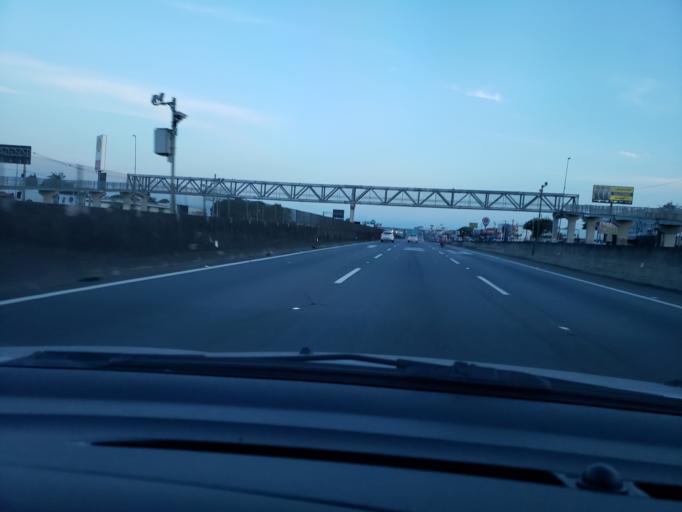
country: BR
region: Sao Paulo
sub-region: Hortolandia
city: Hortolandia
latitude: -22.8506
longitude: -47.1608
